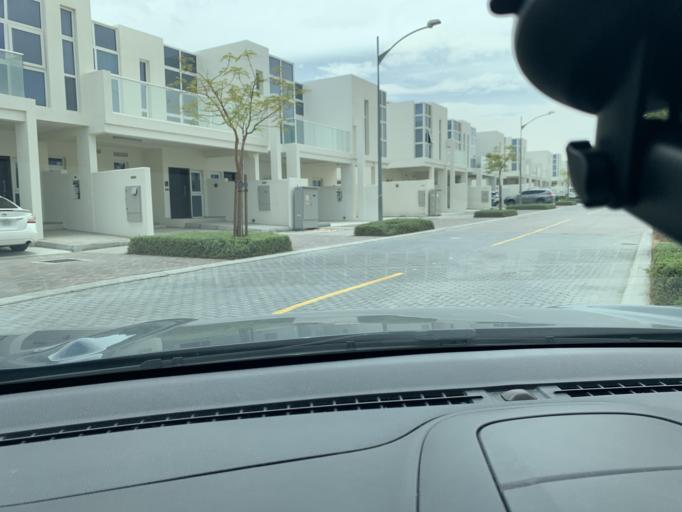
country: AE
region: Dubai
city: Dubai
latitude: 24.9942
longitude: 55.3733
